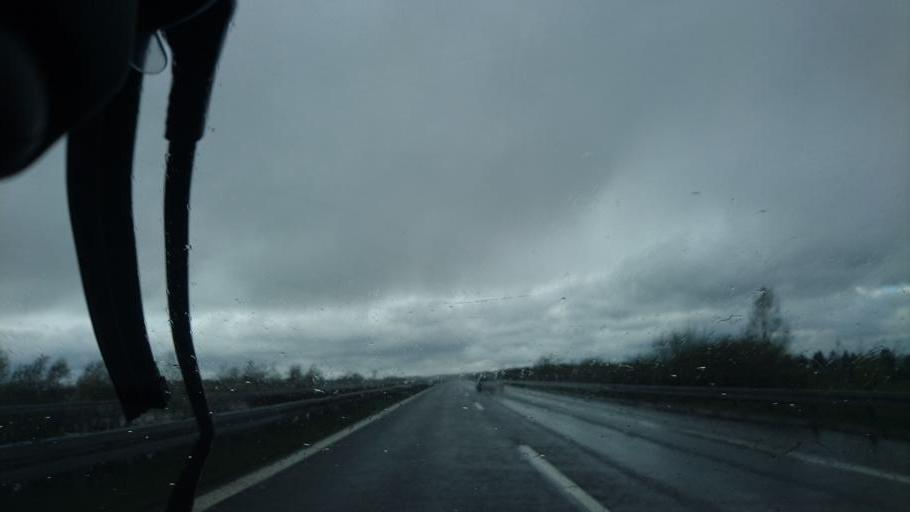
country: DE
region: Mecklenburg-Vorpommern
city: Tessin
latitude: 54.0203
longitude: 12.4311
